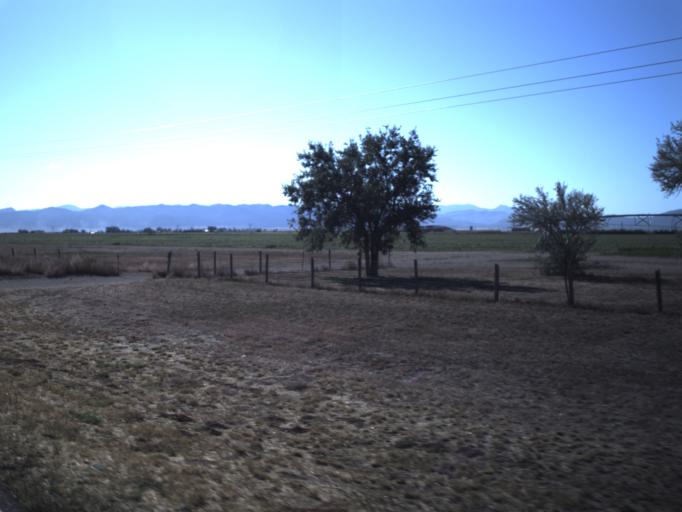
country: US
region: Utah
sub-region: Washington County
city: Enterprise
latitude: 37.7205
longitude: -113.6869
